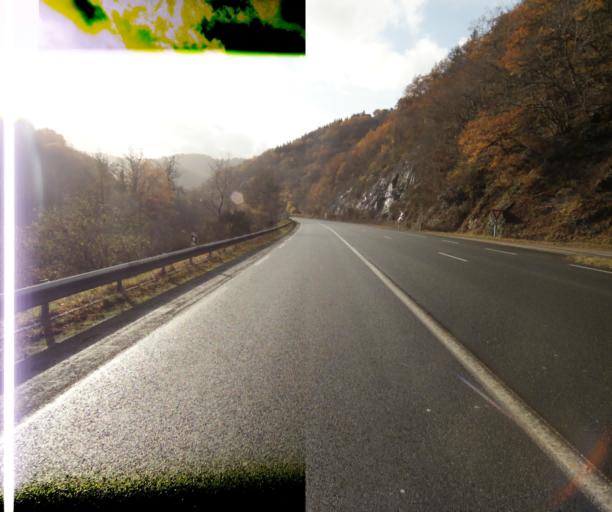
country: FR
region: Limousin
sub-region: Departement de la Correze
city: Cornil
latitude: 45.2124
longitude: 1.6865
